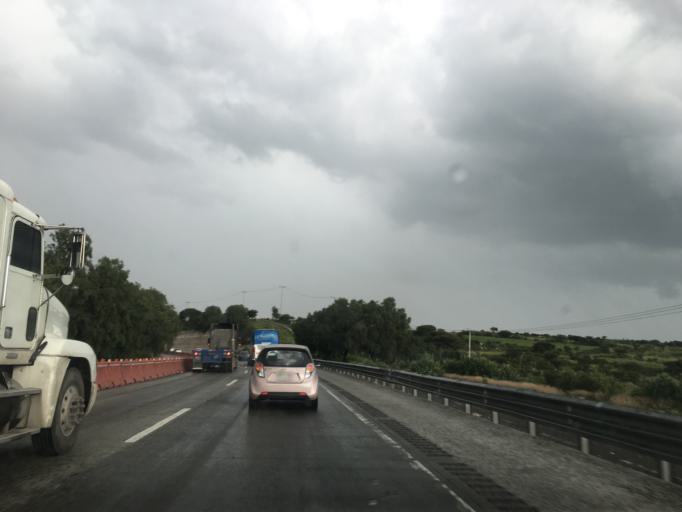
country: MX
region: Hidalgo
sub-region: Tepeji del Rio de Ocampo
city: Cantera de Villagran
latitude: 19.8594
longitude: -99.3142
